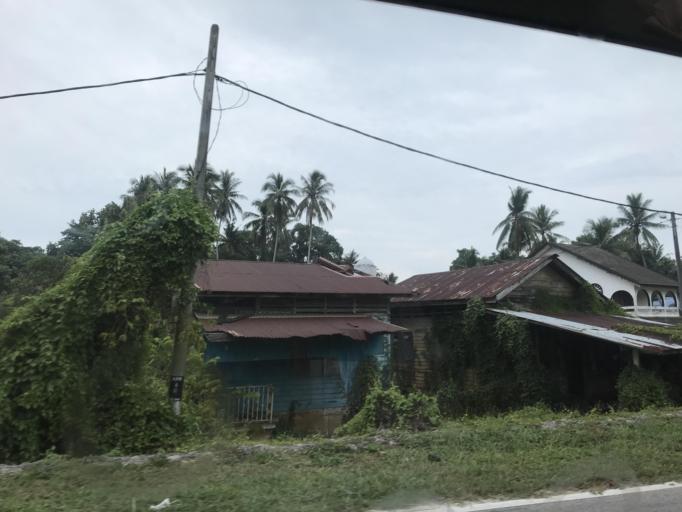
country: MY
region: Kelantan
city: Kota Bharu
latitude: 6.1491
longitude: 102.2285
